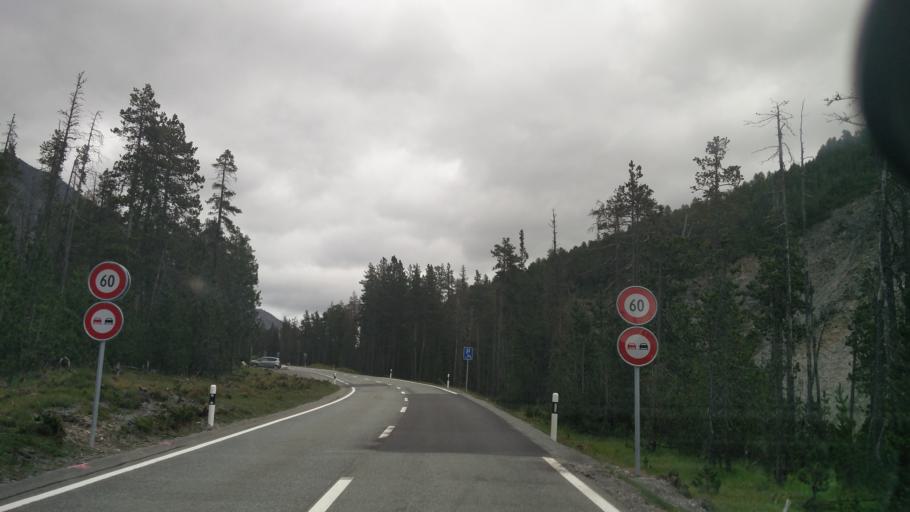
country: CH
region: Grisons
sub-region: Inn District
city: Zernez
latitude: 46.6619
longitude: 10.2218
